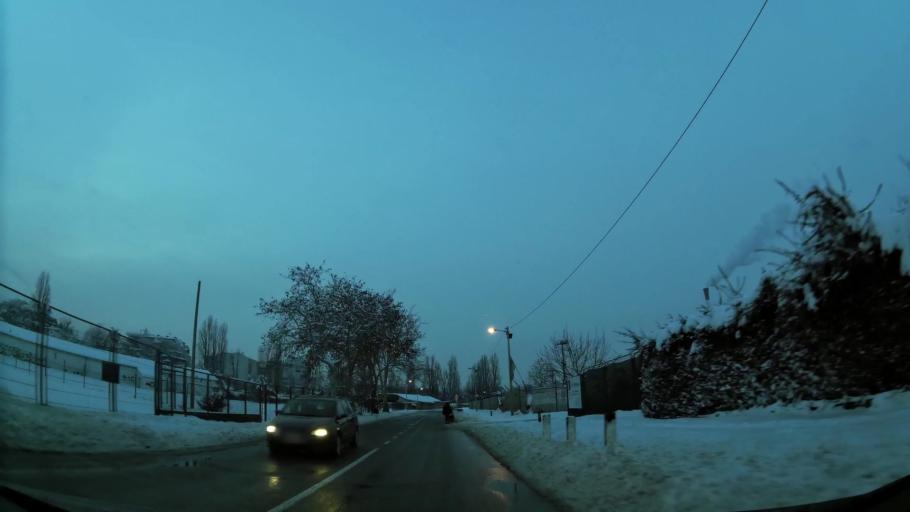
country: RS
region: Central Serbia
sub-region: Belgrade
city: Stari Grad
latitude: 44.8221
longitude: 20.4745
